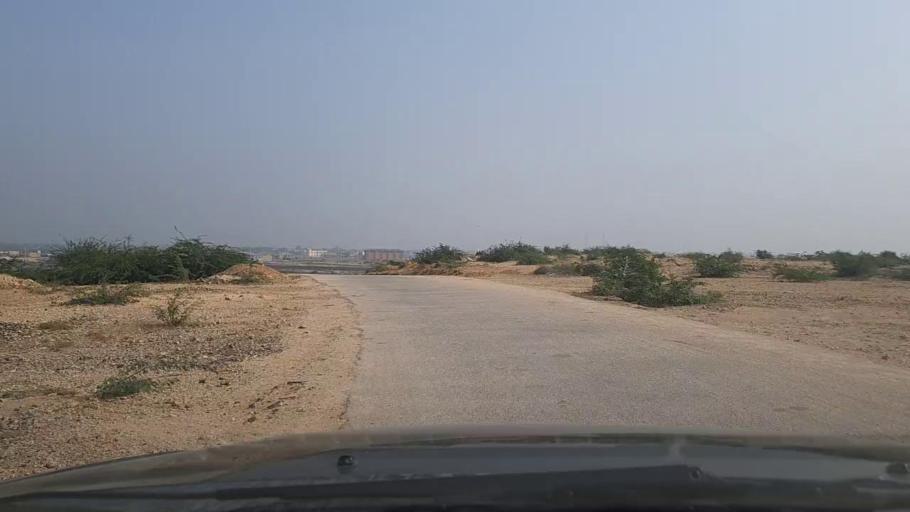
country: PK
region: Sindh
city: Thatta
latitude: 24.7448
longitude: 67.9043
